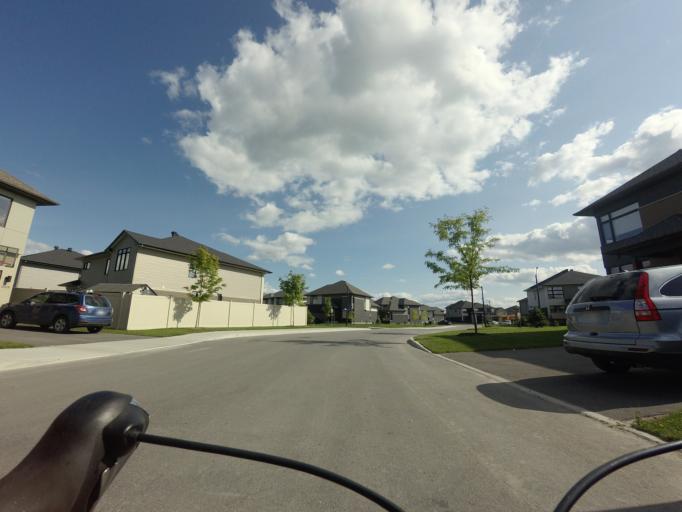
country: CA
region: Ontario
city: Bells Corners
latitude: 45.2857
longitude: -75.8417
